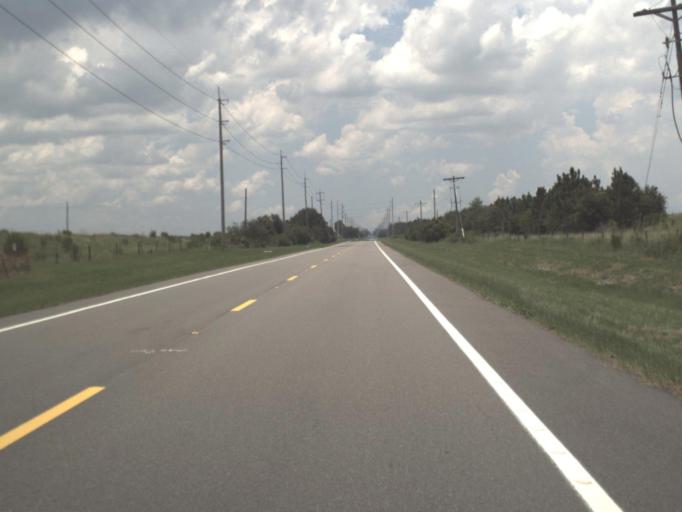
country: US
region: Florida
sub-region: Hillsborough County
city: Boyette
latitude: 27.7045
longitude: -82.1116
